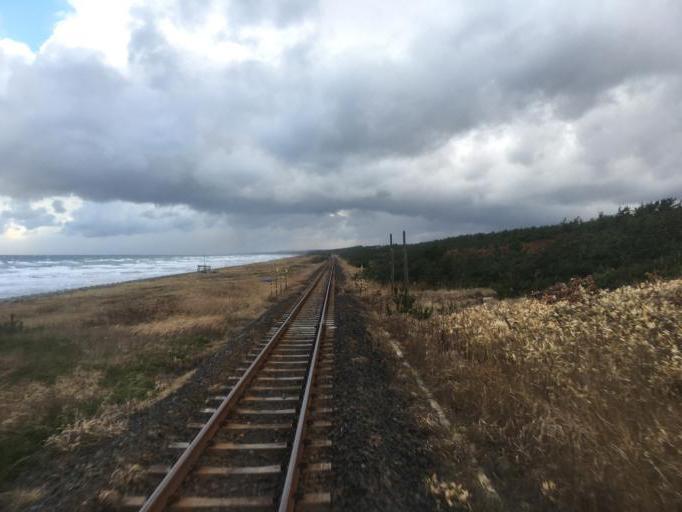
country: JP
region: Aomori
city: Mutsu
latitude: 40.9785
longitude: 141.2245
